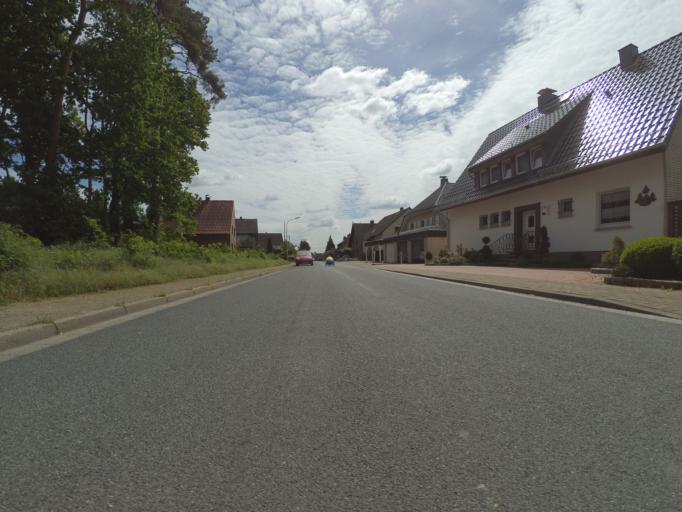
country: DE
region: Lower Saxony
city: Wunstorf
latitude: 52.4631
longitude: 9.3945
